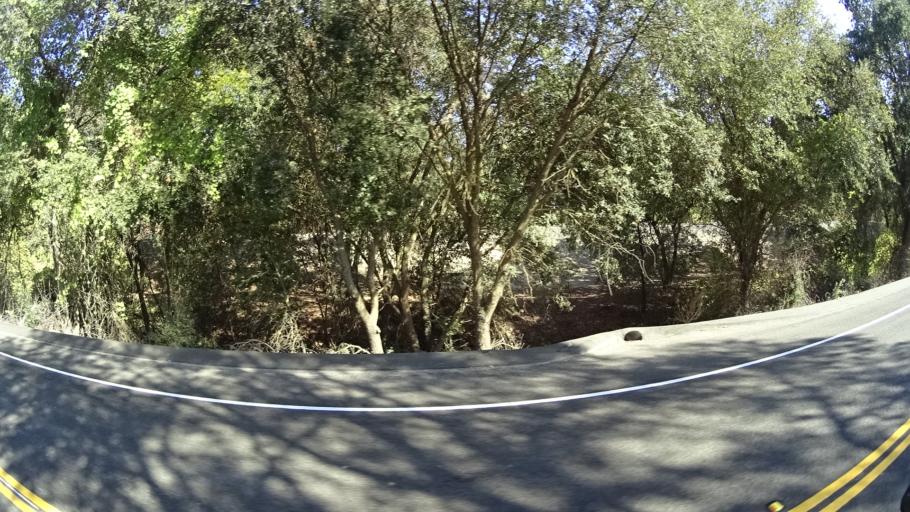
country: US
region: California
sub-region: Yolo County
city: West Sacramento
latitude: 38.6621
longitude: -121.6155
